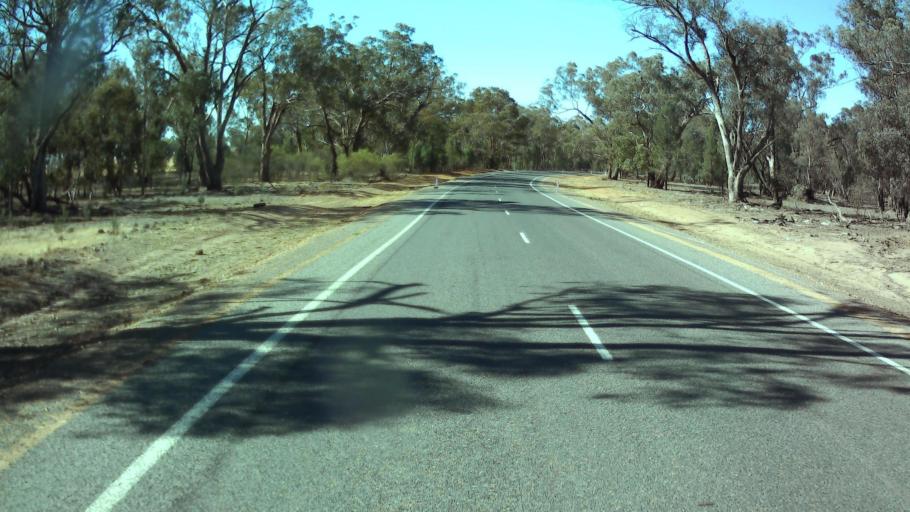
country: AU
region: New South Wales
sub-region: Weddin
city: Grenfell
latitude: -33.7566
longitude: 148.0826
